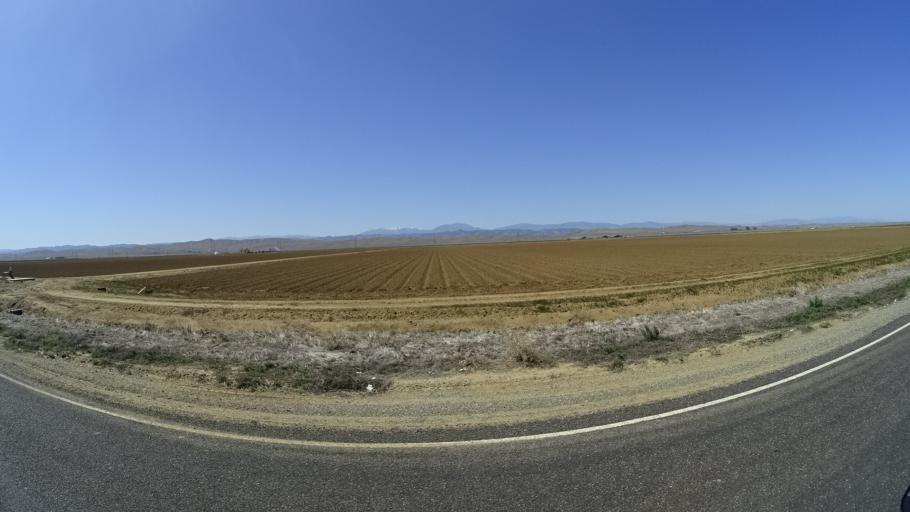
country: US
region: California
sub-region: Glenn County
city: Willows
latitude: 39.4184
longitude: -122.2484
